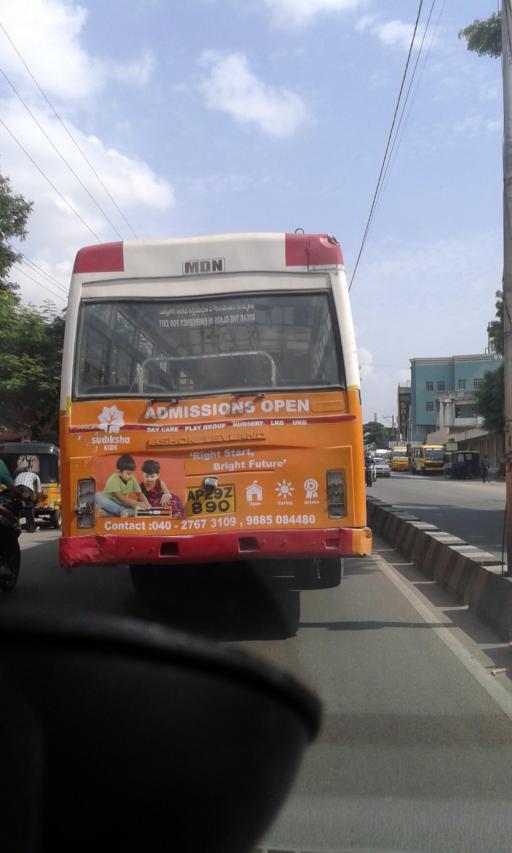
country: IN
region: Telangana
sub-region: Rangareddi
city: Gaddi Annaram
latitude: 17.3563
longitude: 78.5056
